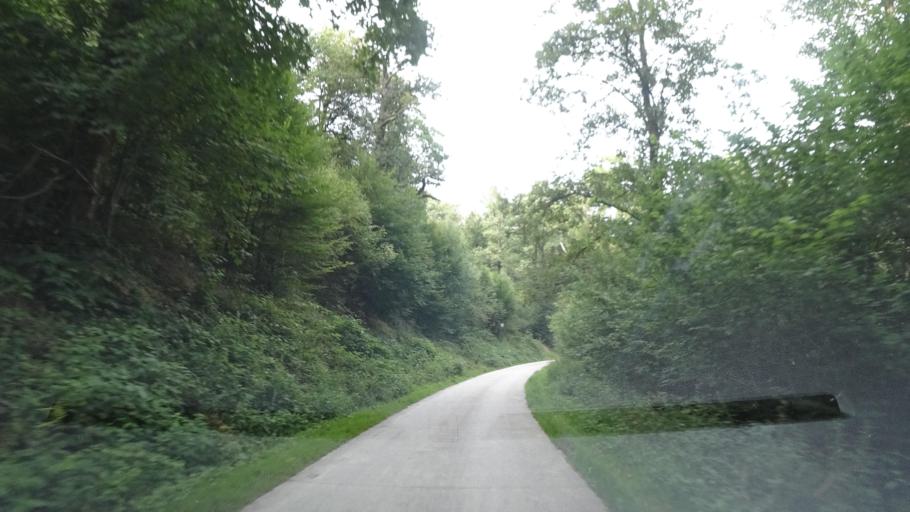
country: BE
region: Wallonia
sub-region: Province du Luxembourg
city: Herbeumont
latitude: 49.7705
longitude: 5.2527
